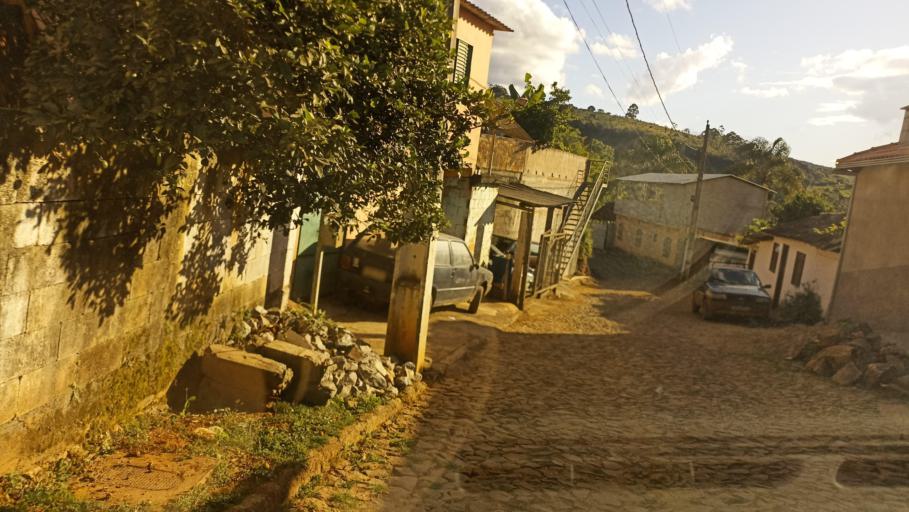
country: BR
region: Minas Gerais
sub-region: Ouro Preto
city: Ouro Preto
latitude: -20.3096
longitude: -43.5783
